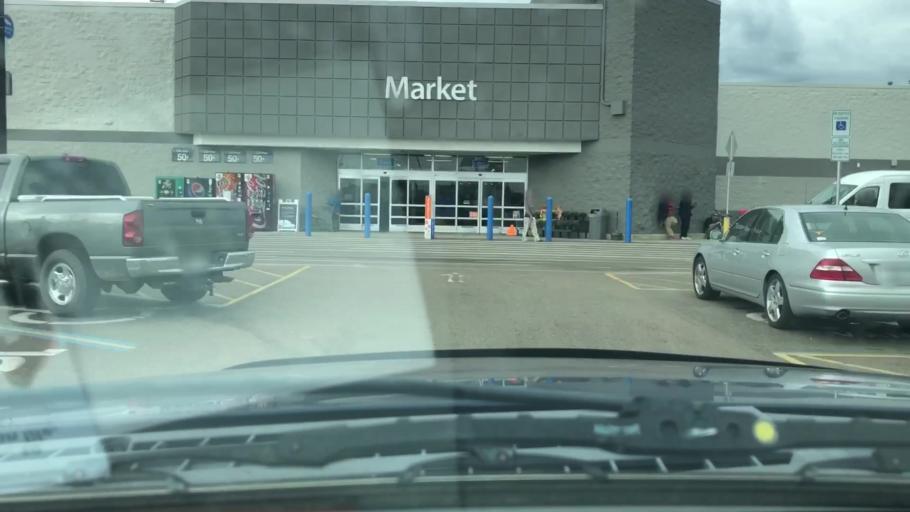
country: US
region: Texas
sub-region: Bowie County
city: Wake Village
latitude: 33.4456
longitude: -94.1003
